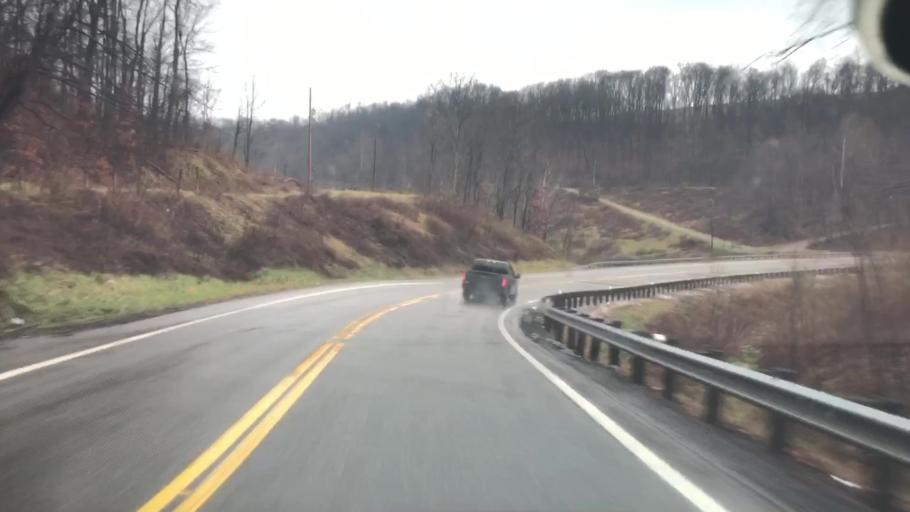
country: US
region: Ohio
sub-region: Belmont County
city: Saint Clairsville
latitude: 40.1121
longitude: -80.9326
